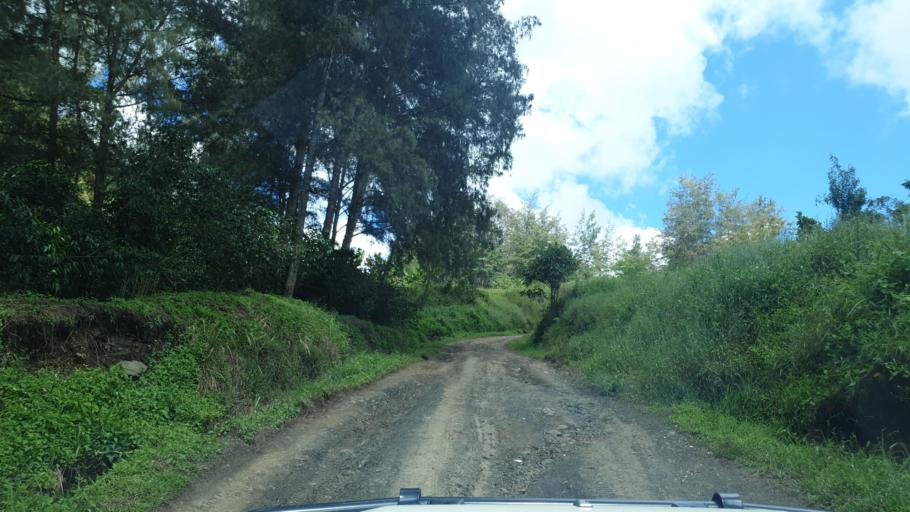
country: PG
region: Chimbu
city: Kundiawa
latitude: -6.2591
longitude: 145.1380
